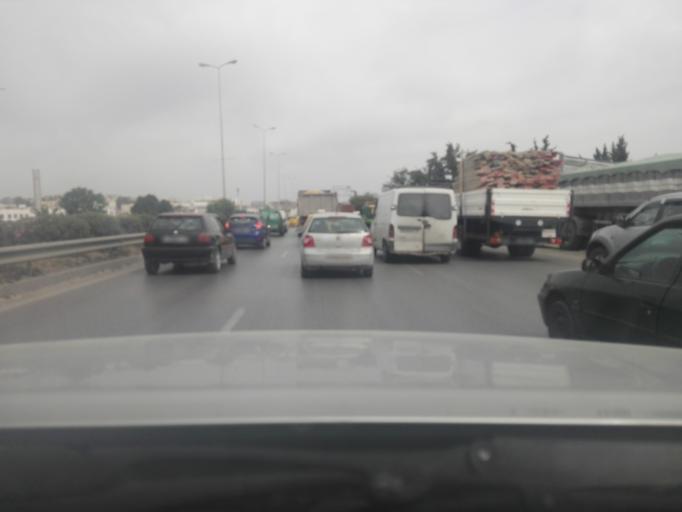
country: TN
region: Bin 'Arus
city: Ben Arous
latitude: 36.7571
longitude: 10.2009
